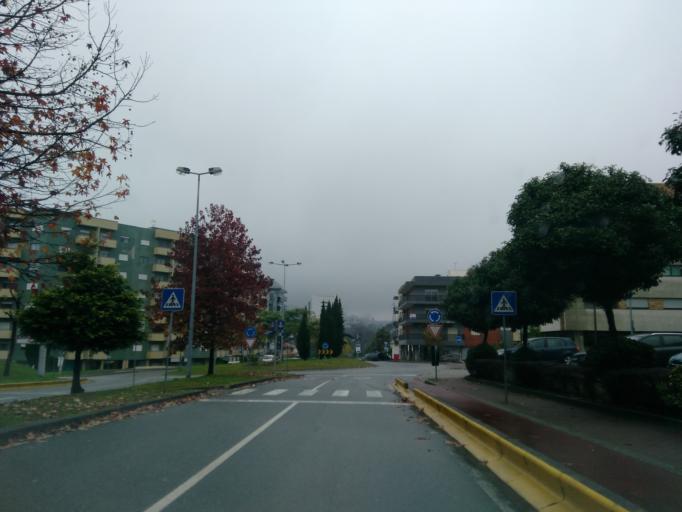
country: PT
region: Braga
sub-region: Braga
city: Braga
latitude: 41.5525
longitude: -8.3953
